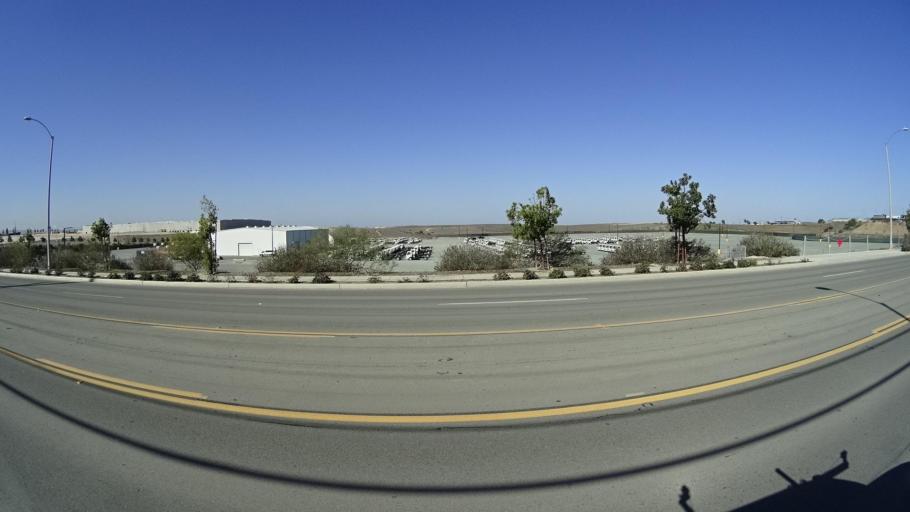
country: MX
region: Baja California
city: Tijuana
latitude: 32.5727
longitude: -116.9191
